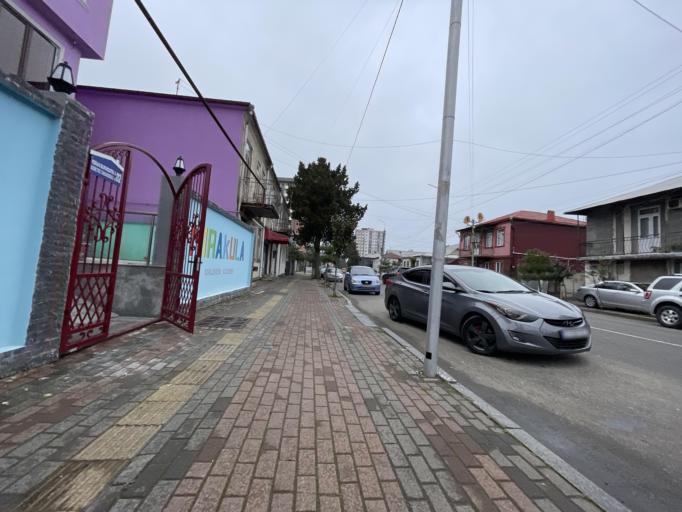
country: GE
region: Ajaria
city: Batumi
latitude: 41.6388
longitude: 41.6423
